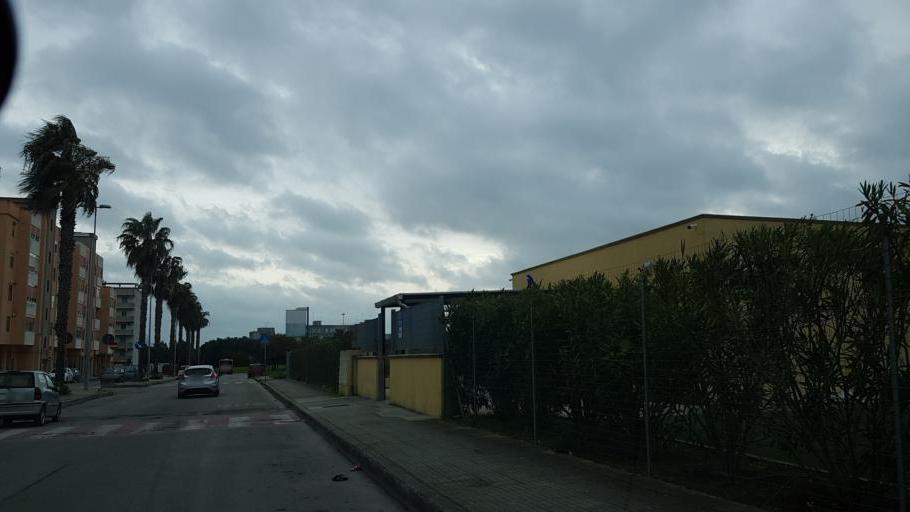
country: IT
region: Apulia
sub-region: Provincia di Brindisi
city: Brindisi
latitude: 40.6191
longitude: 17.9312
